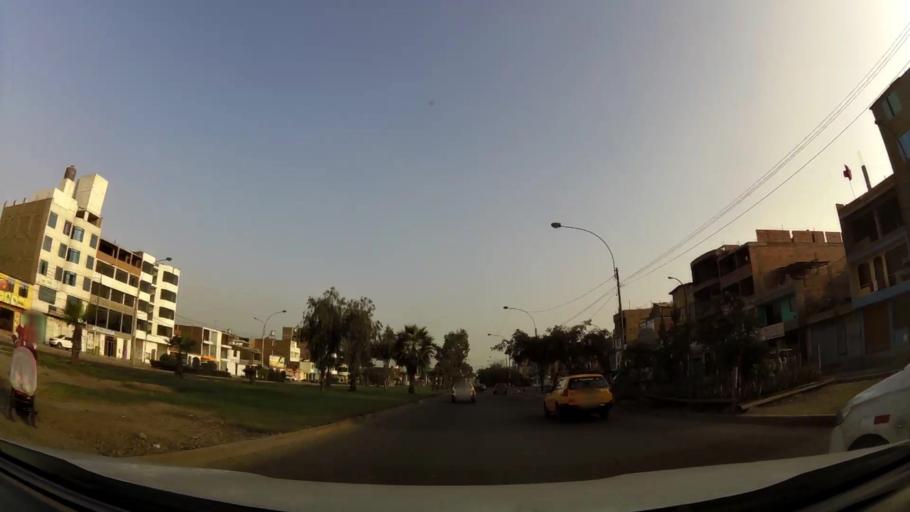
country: PE
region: Lima
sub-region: Lima
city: Independencia
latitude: -11.9682
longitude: -77.0751
